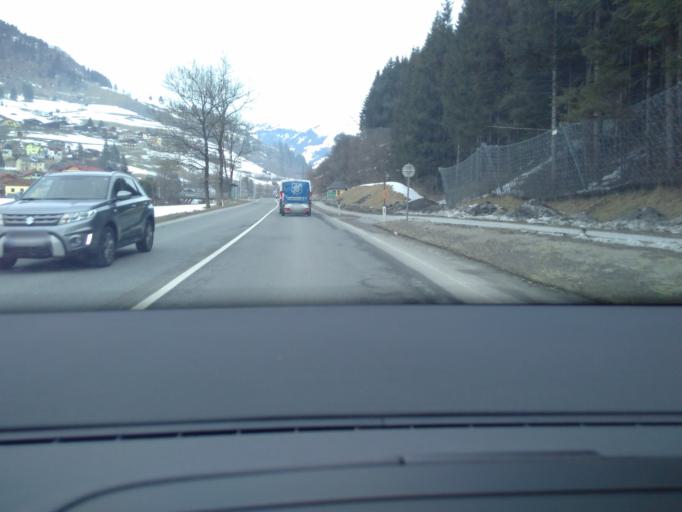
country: AT
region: Salzburg
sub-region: Politischer Bezirk Sankt Johann im Pongau
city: Bad Hofgastein
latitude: 47.1916
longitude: 13.1021
